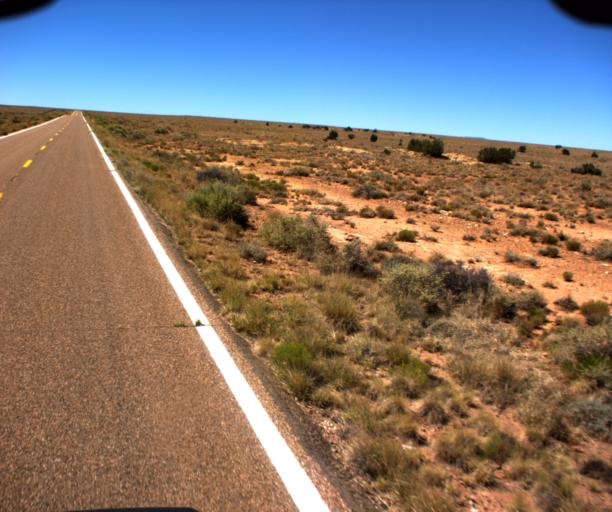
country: US
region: Arizona
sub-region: Navajo County
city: Winslow
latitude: 34.9277
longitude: -110.6378
